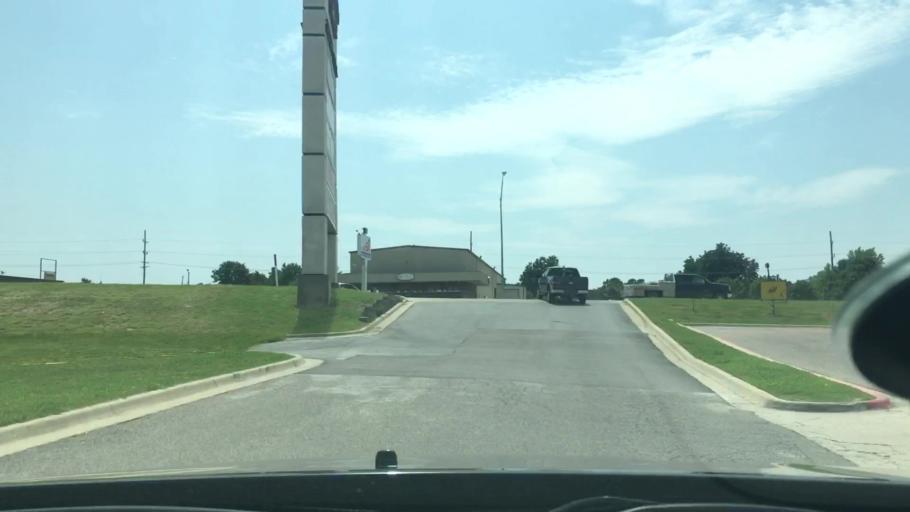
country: US
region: Oklahoma
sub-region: Pontotoc County
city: Ada
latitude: 34.7908
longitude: -96.6645
